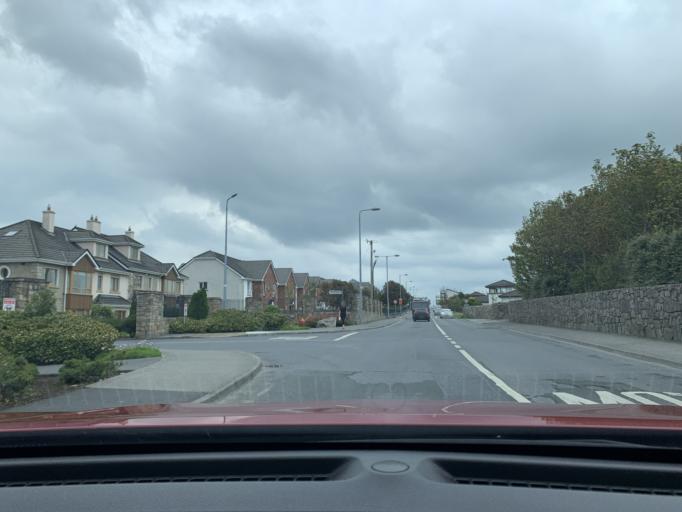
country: IE
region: Connaught
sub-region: County Galway
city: Bearna
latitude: 53.2713
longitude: -9.1177
